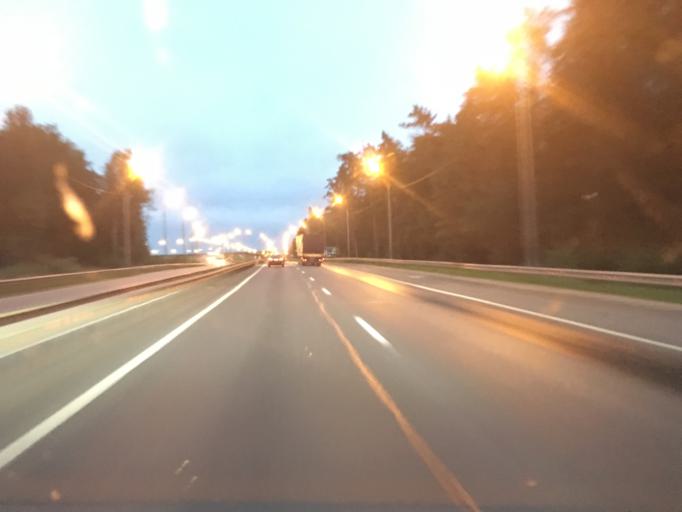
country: RU
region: Kaluga
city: Maloyaroslavets
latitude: 54.9741
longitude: 36.4850
